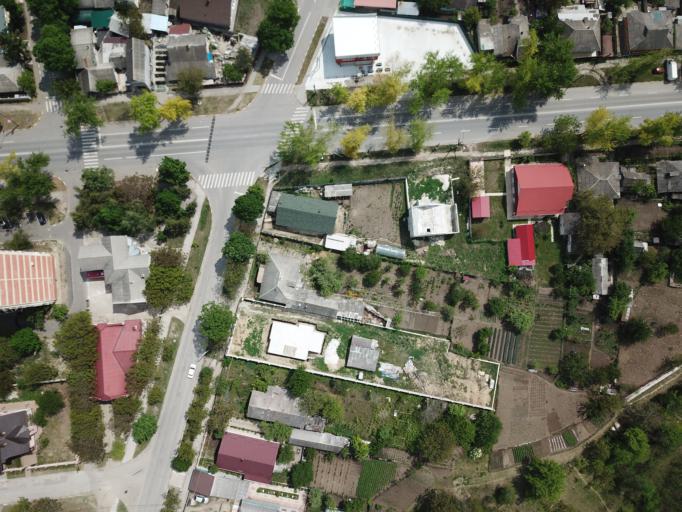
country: MD
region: Ungheni
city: Ungheni
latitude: 47.2076
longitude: 27.7937
